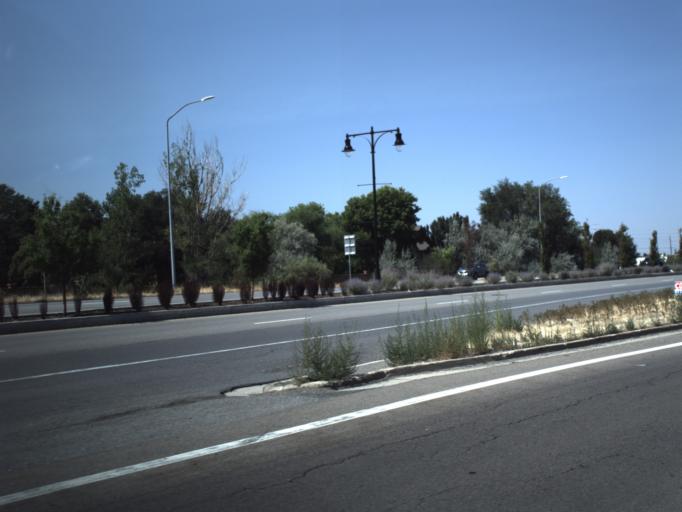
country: US
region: Utah
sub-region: Salt Lake County
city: Little Cottonwood Creek Valley
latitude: 40.6267
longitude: -111.8615
